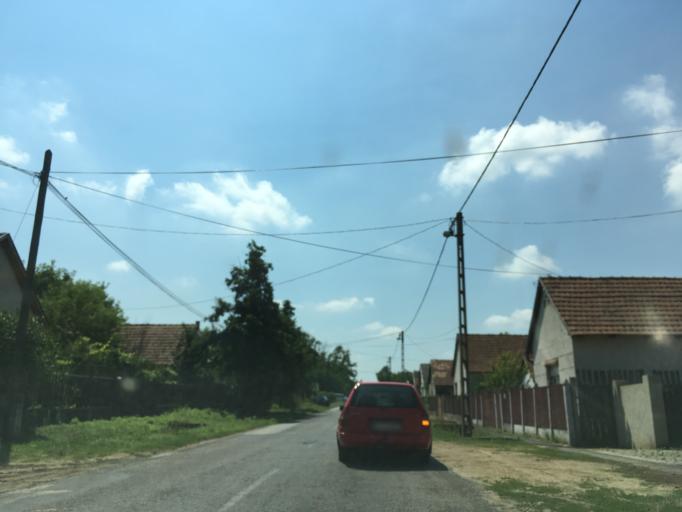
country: HU
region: Szabolcs-Szatmar-Bereg
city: Nyirlugos
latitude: 47.6778
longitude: 22.0451
